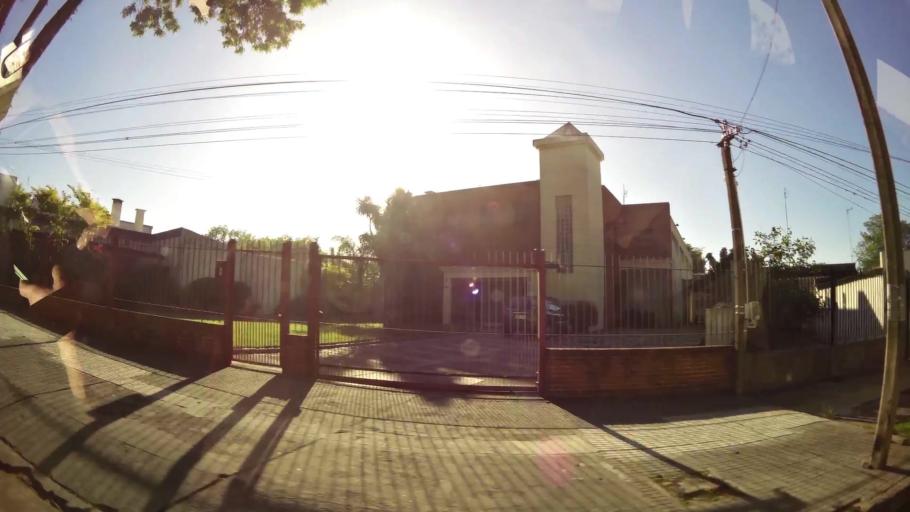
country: UY
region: Montevideo
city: Montevideo
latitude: -34.8419
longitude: -56.2013
